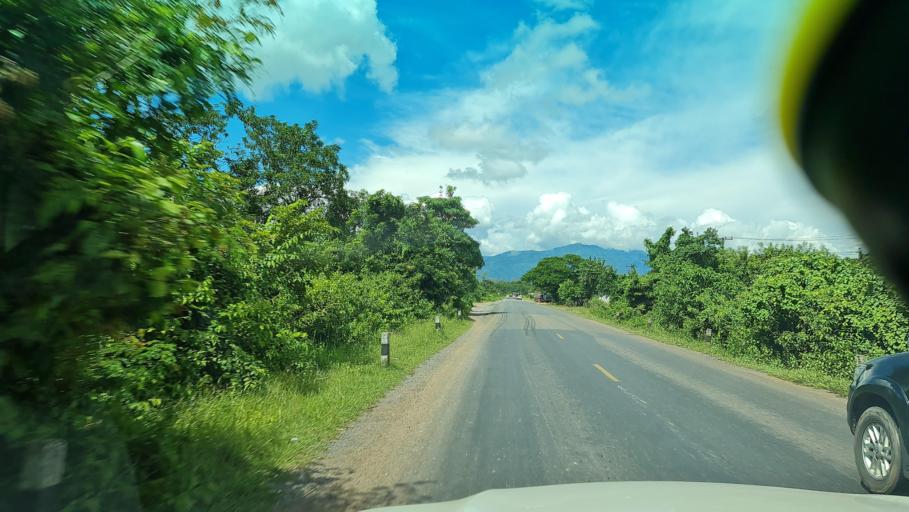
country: LA
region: Bolikhamxai
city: Pakkading
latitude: 18.2802
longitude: 104.0672
